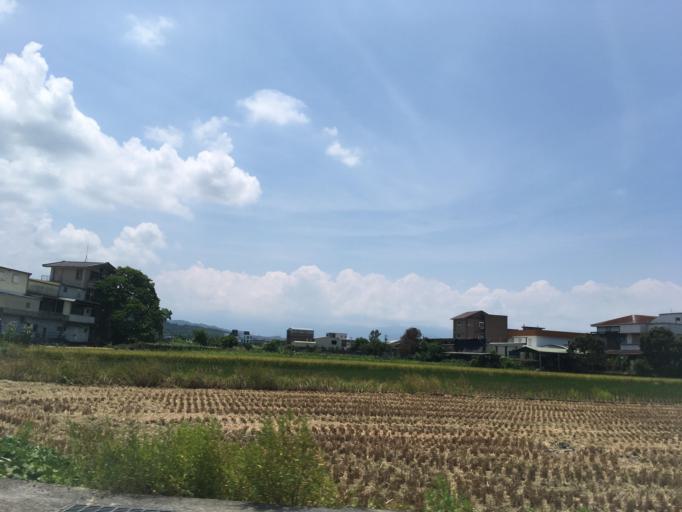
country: TW
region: Taiwan
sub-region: Yilan
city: Yilan
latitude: 24.6453
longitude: 121.7641
